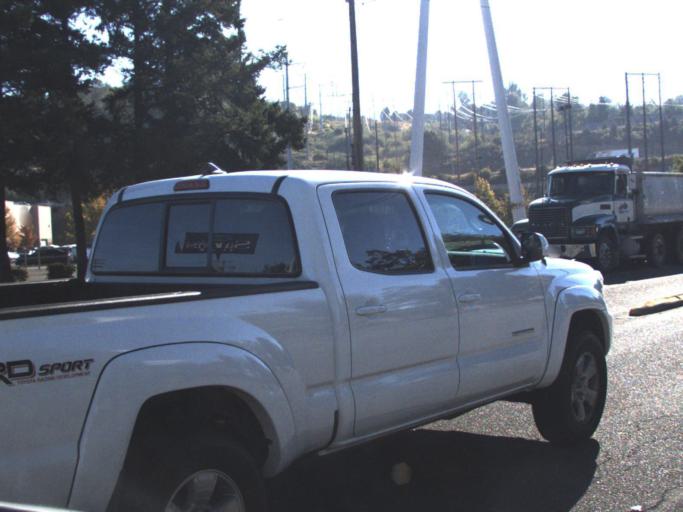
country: US
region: Washington
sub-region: King County
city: Renton
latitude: 47.4724
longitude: -122.2084
